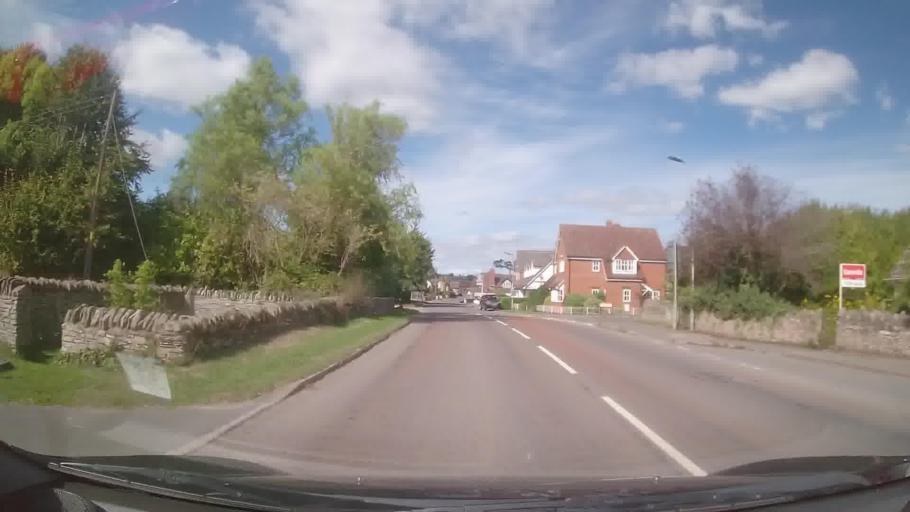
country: GB
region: England
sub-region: Herefordshire
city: Kinnersley
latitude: 52.1371
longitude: -3.0058
